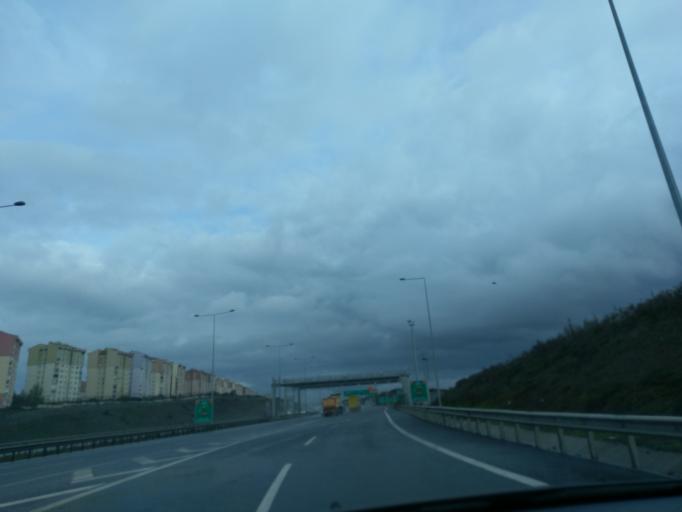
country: TR
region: Istanbul
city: Basaksehir
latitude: 41.0857
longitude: 28.8137
